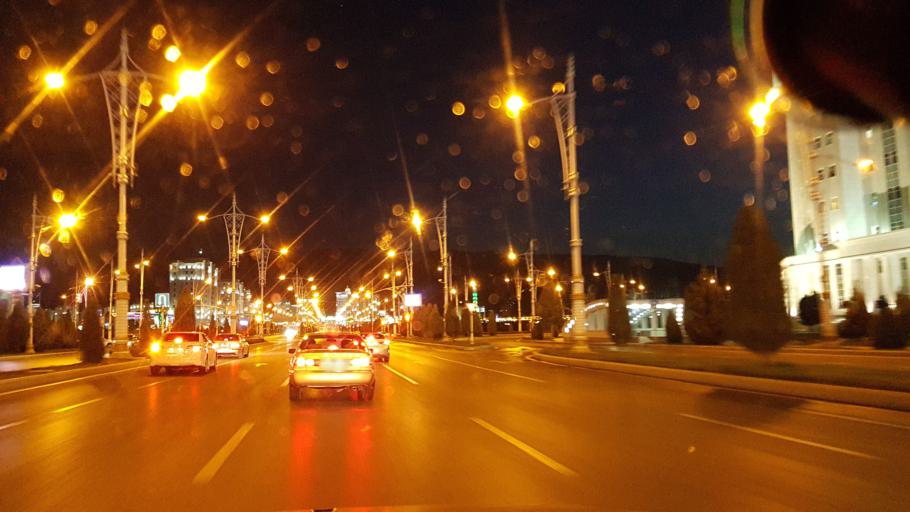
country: TM
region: Ahal
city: Ashgabat
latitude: 37.9147
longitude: 58.3441
